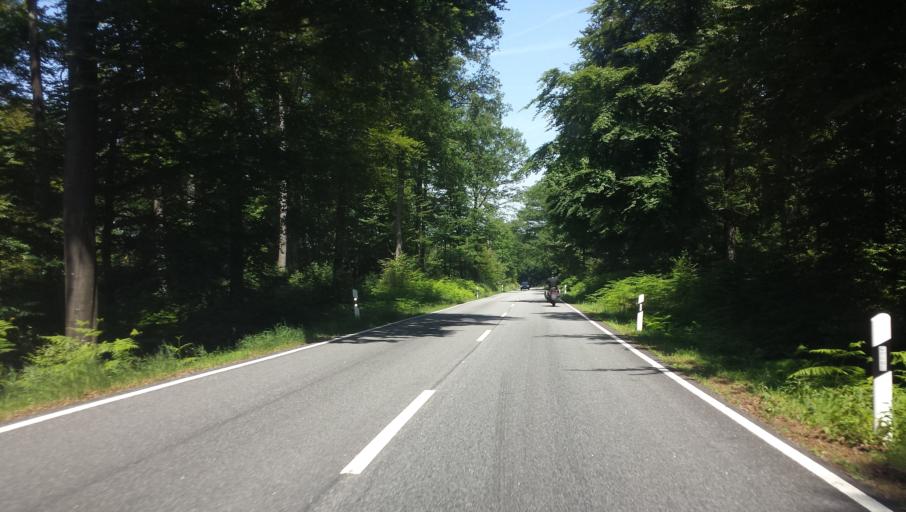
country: DE
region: Rheinland-Pfalz
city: Waldleiningen
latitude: 49.3704
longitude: 7.8491
